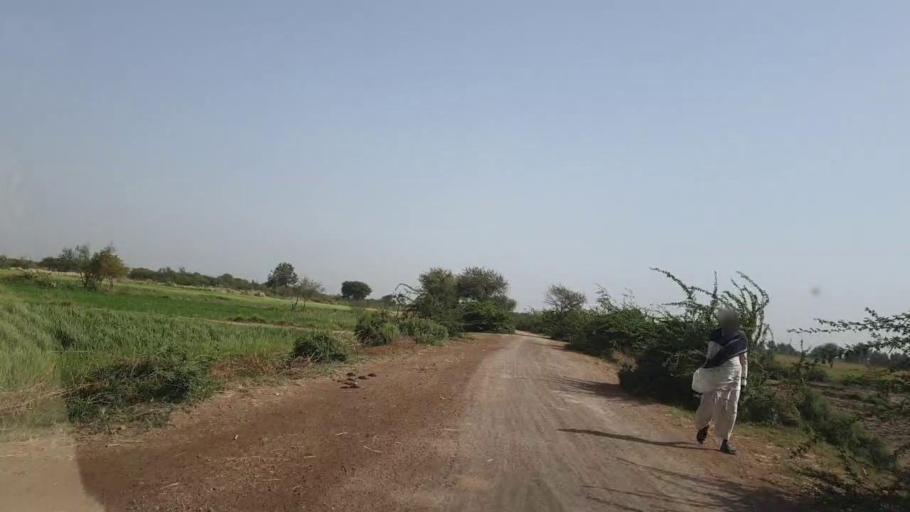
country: PK
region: Sindh
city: Rajo Khanani
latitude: 25.0394
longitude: 68.8512
